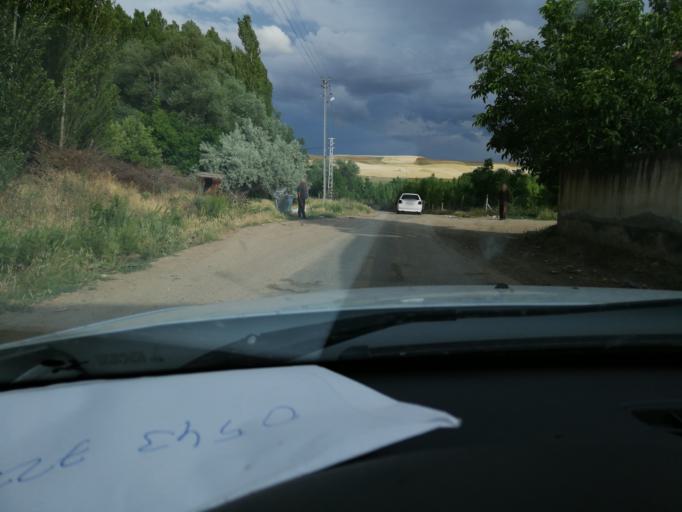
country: TR
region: Kirsehir
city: Kirsehir
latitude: 39.0286
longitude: 34.1295
